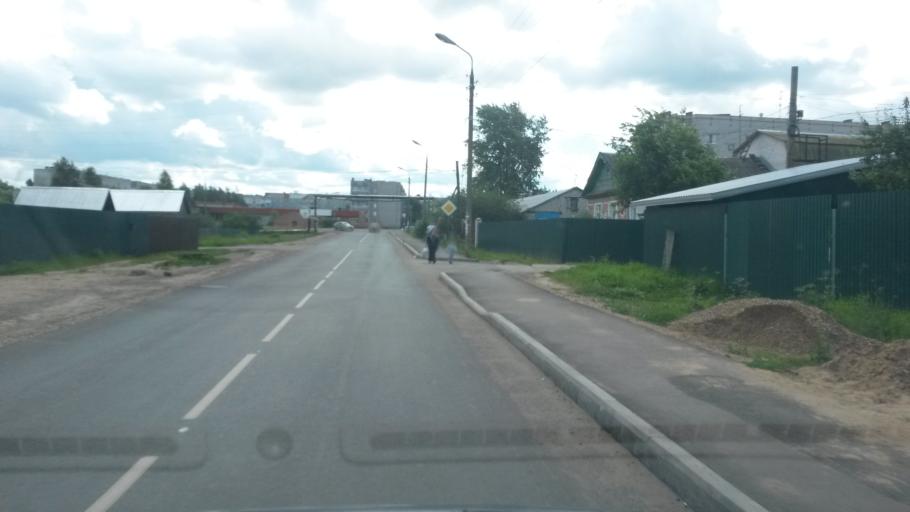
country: RU
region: Jaroslavl
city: Gavrilov-Yam
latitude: 57.3088
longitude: 39.8668
